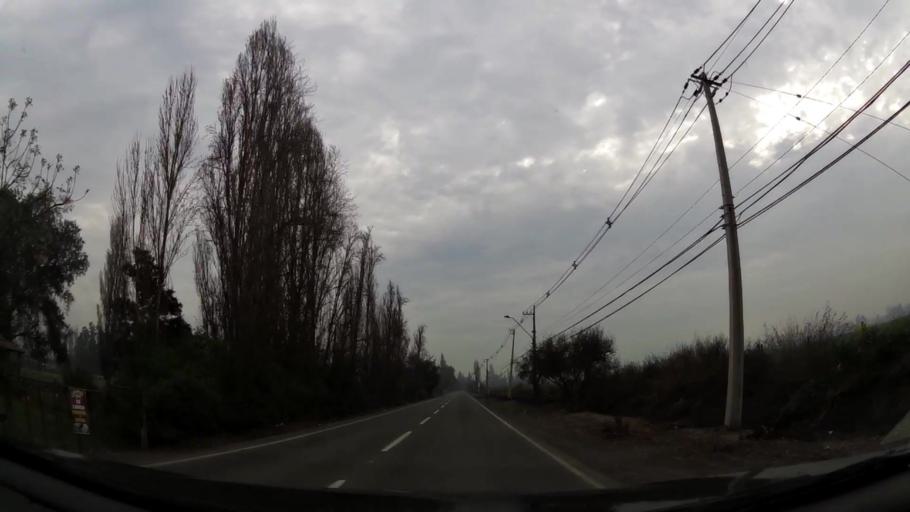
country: CL
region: Santiago Metropolitan
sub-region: Provincia de Chacabuco
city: Chicureo Abajo
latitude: -33.2536
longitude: -70.7631
